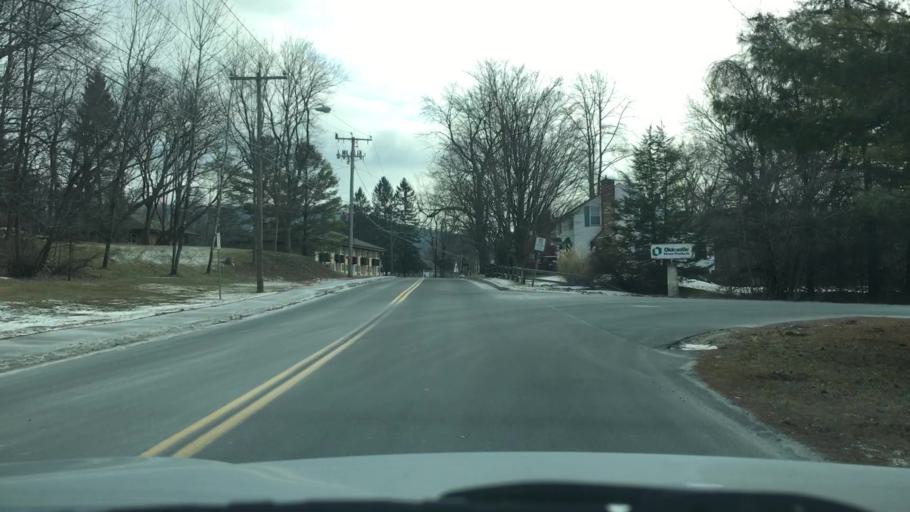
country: US
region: Massachusetts
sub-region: Berkshire County
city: Lee
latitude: 42.3009
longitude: -73.2510
